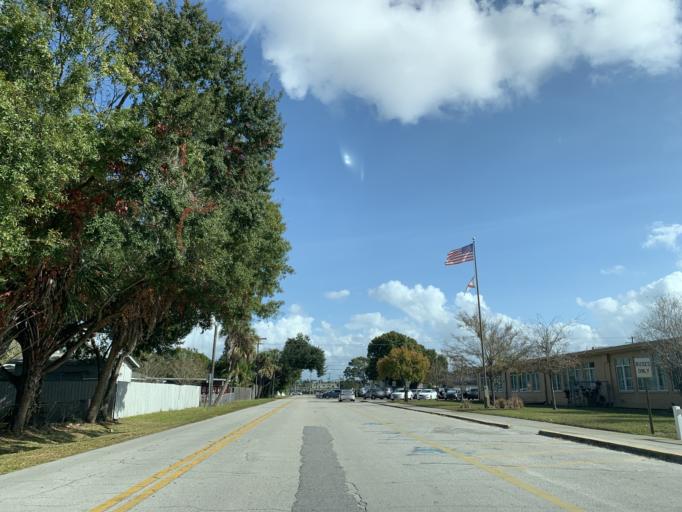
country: US
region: Florida
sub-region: Hillsborough County
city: Tampa
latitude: 27.9069
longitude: -82.5208
